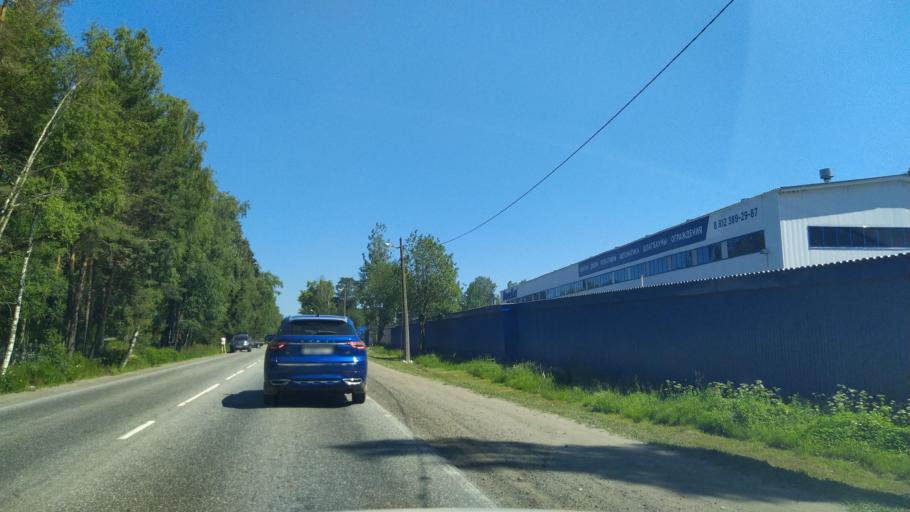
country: RU
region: Leningrad
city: Imeni Morozova
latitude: 59.9663
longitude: 31.0158
